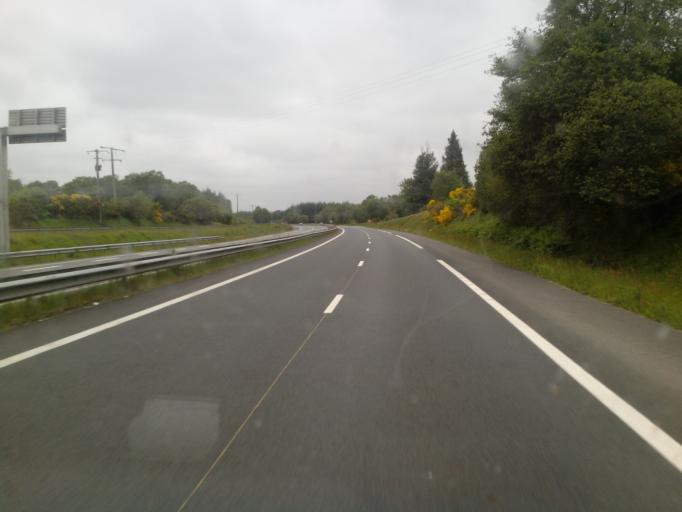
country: FR
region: Brittany
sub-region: Departement du Finistere
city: Guerlesquin
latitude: 48.5662
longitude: -3.5476
